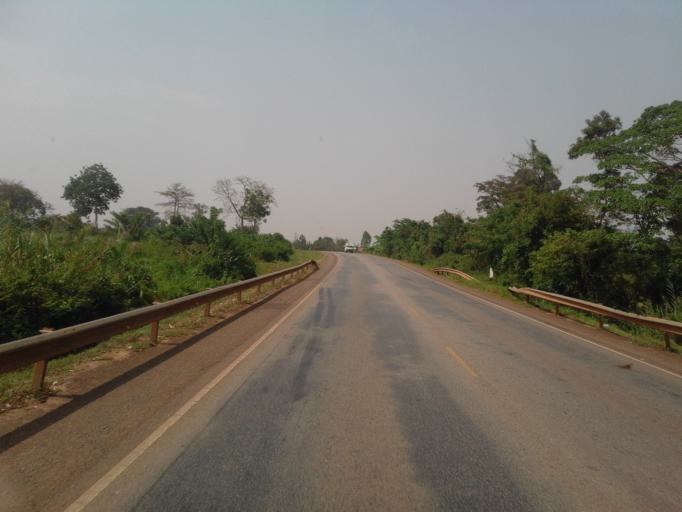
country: UG
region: Eastern Region
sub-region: Iganga District
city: Iganga
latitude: 0.5825
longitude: 33.4318
